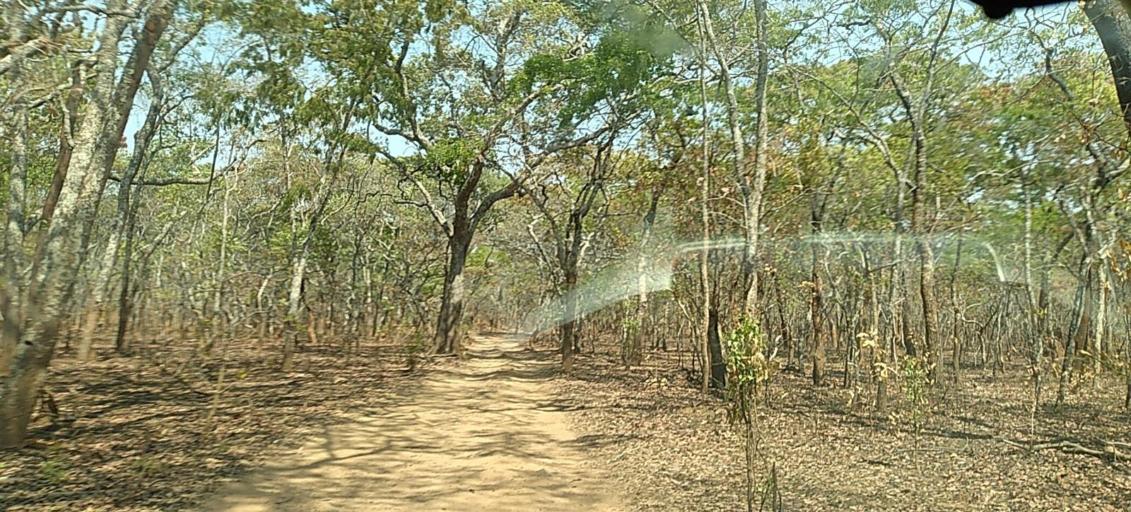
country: ZM
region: North-Western
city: Kasempa
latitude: -13.3936
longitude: 25.5953
